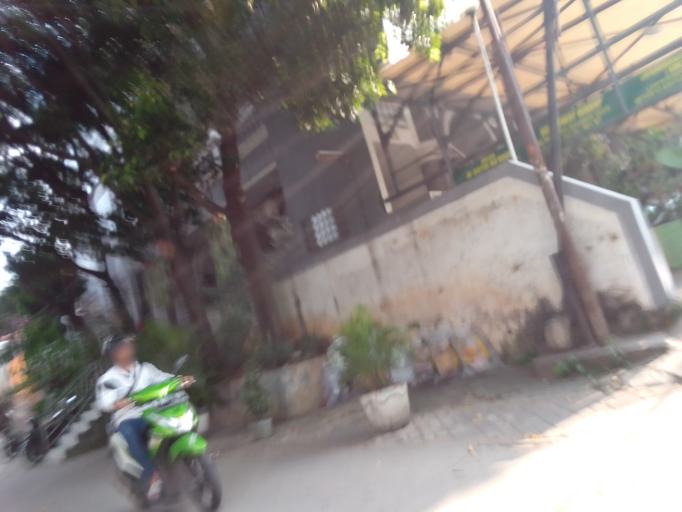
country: ID
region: Jakarta Raya
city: Jakarta
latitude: -6.2581
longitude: 106.7906
